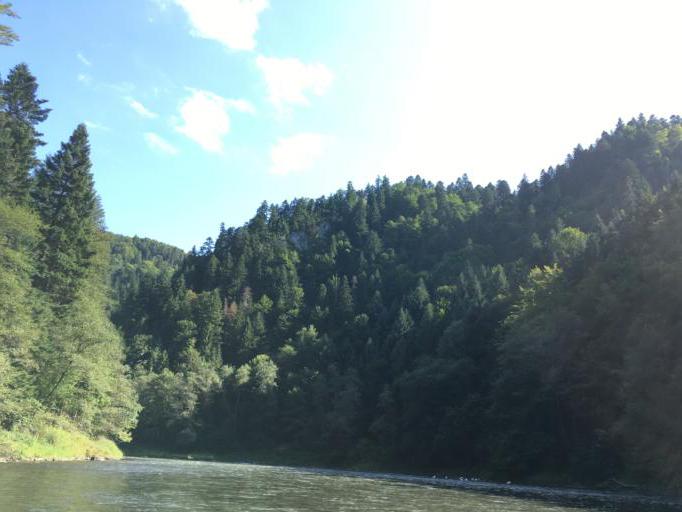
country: PL
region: Lesser Poland Voivodeship
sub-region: Powiat nowotarski
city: Kroscienko nad Dunajcem
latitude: 49.3971
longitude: 20.4304
